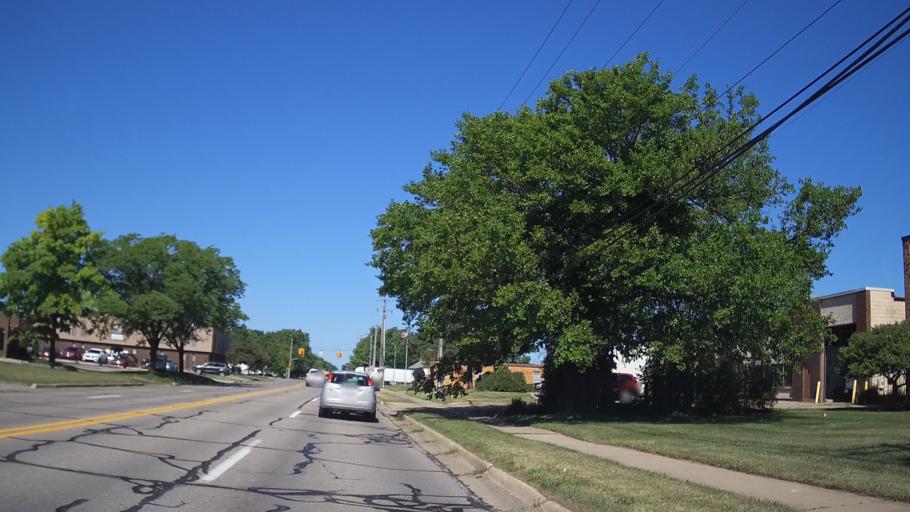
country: US
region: Michigan
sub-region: Macomb County
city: Fraser
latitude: 42.5316
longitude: -82.9464
